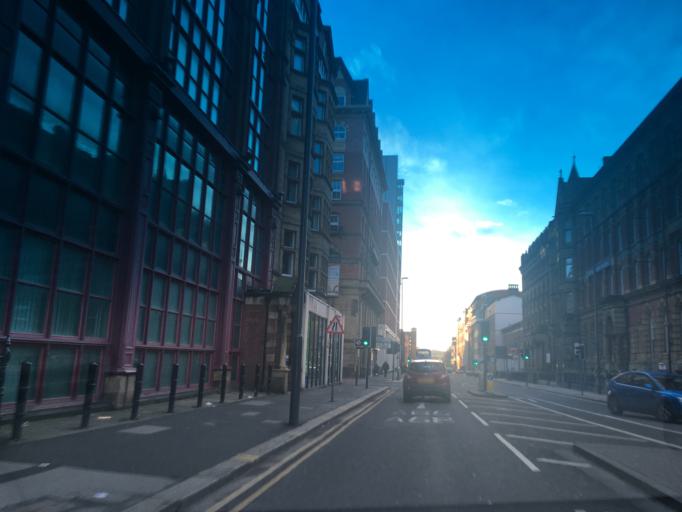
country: GB
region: England
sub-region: City and Borough of Leeds
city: Leeds
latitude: 53.7963
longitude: -1.5504
